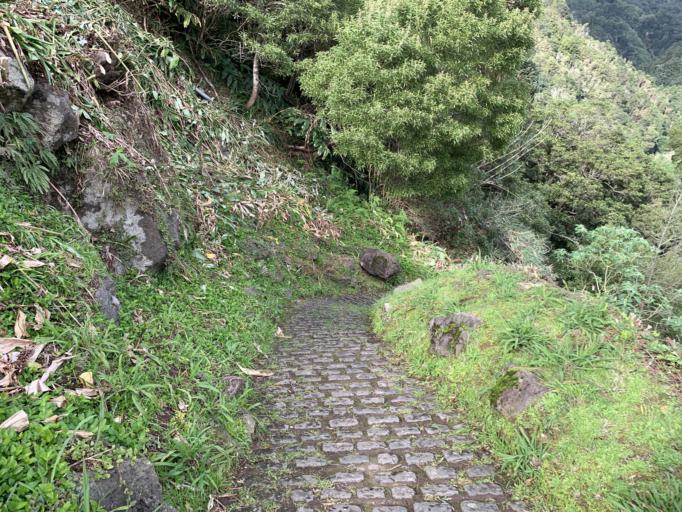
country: PT
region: Azores
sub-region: Povoacao
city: Furnas
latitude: 37.7511
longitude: -25.2032
